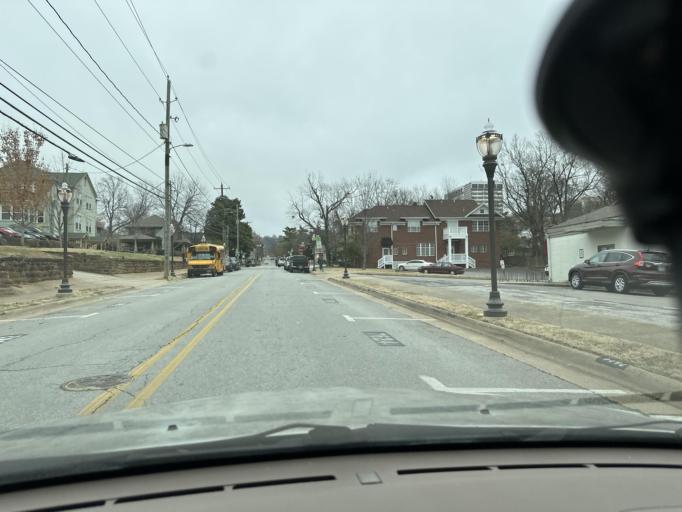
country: US
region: Arkansas
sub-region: Washington County
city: Fayetteville
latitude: 36.0647
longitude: -94.1627
